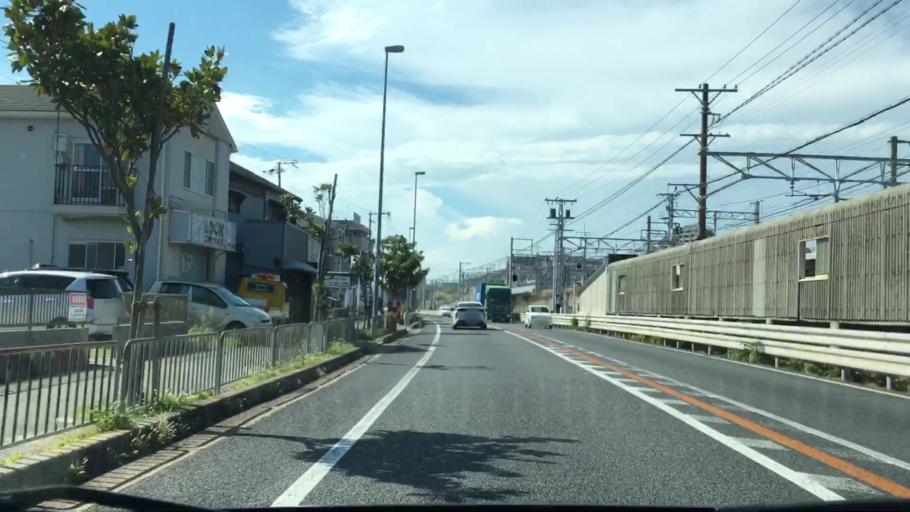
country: JP
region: Hyogo
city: Akashi
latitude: 34.6386
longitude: 135.0280
